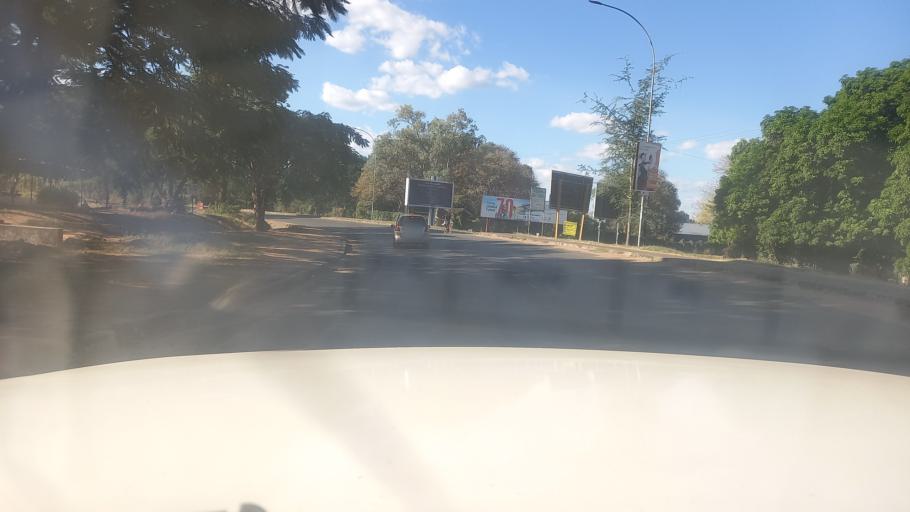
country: ZM
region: Southern
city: Livingstone
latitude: -17.8396
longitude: 25.8640
